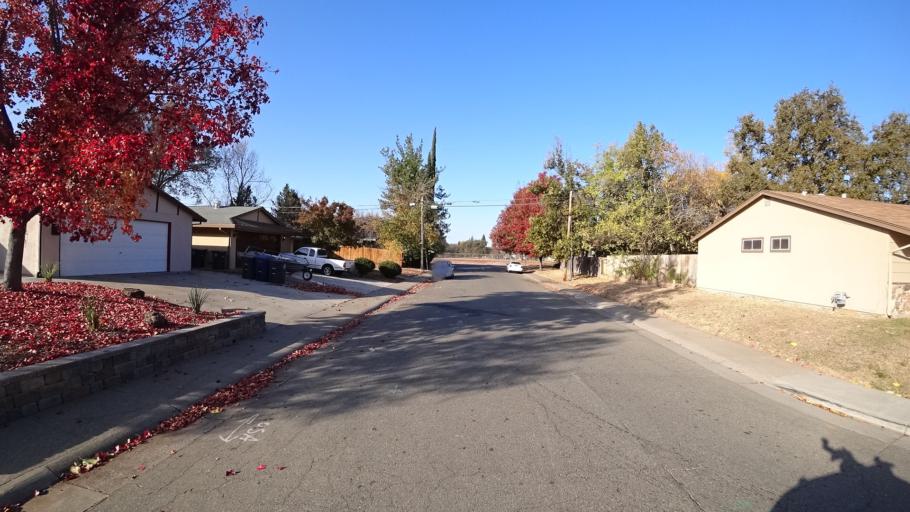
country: US
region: California
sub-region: Sacramento County
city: Citrus Heights
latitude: 38.6988
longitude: -121.2686
